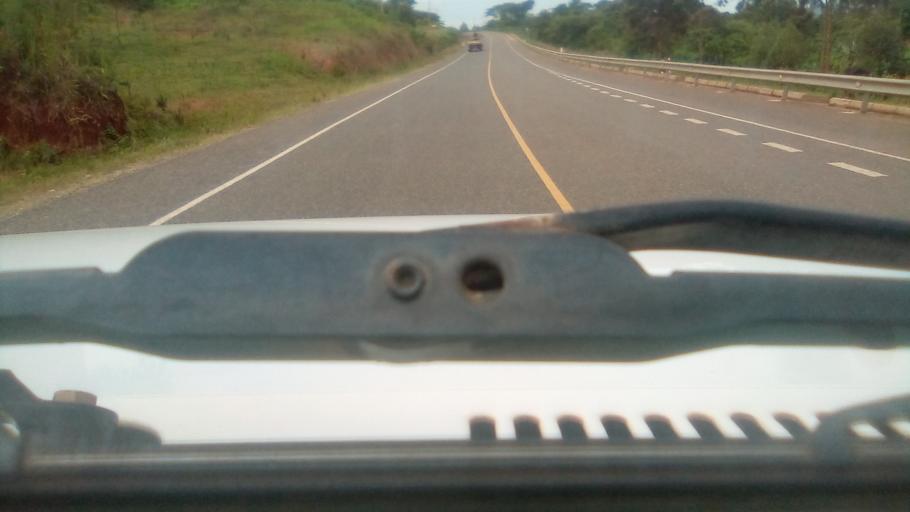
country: UG
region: Eastern Region
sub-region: Mbale District
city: Mbale
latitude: 0.9604
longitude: 34.2126
